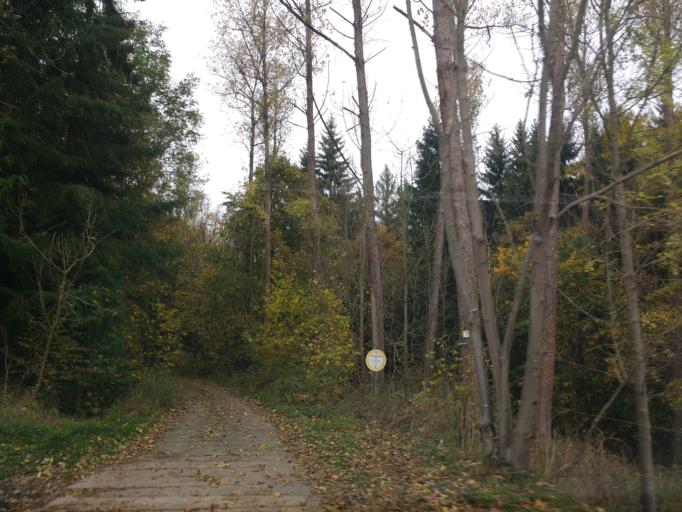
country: DE
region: Thuringia
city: Buhla
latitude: 51.4280
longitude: 10.4132
